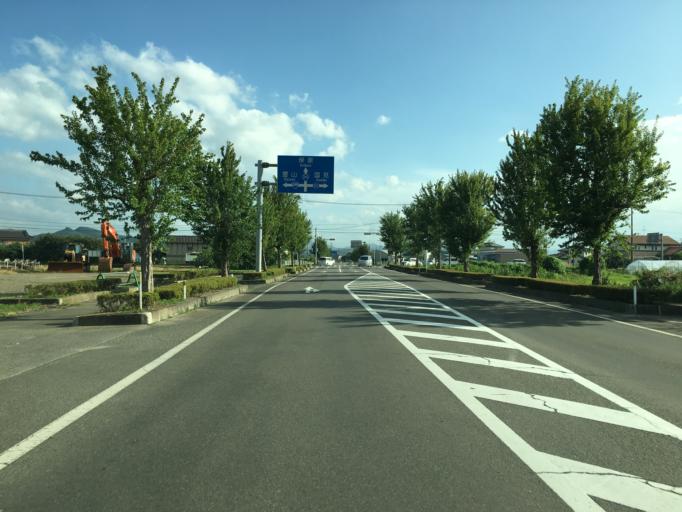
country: JP
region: Fukushima
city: Yanagawamachi-saiwaicho
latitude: 37.8512
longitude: 140.5924
